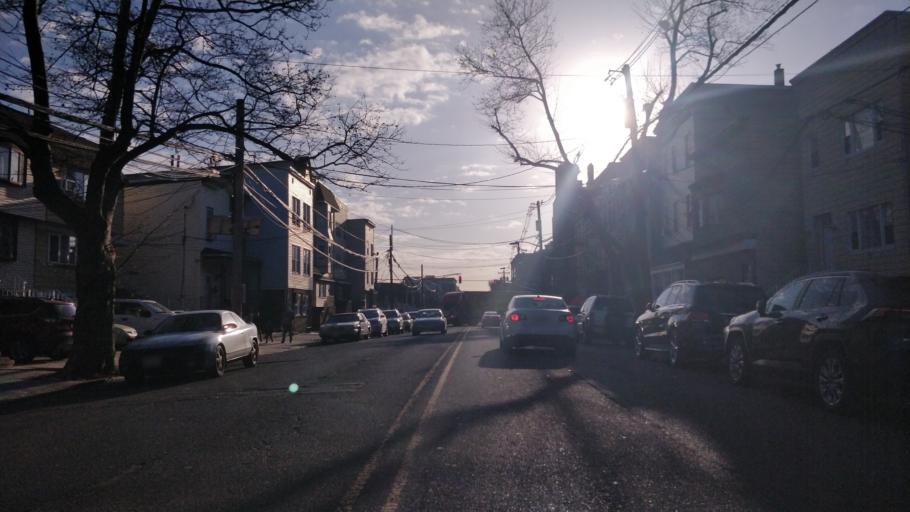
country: US
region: New Jersey
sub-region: Hudson County
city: Bayonne
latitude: 40.6652
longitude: -74.1140
